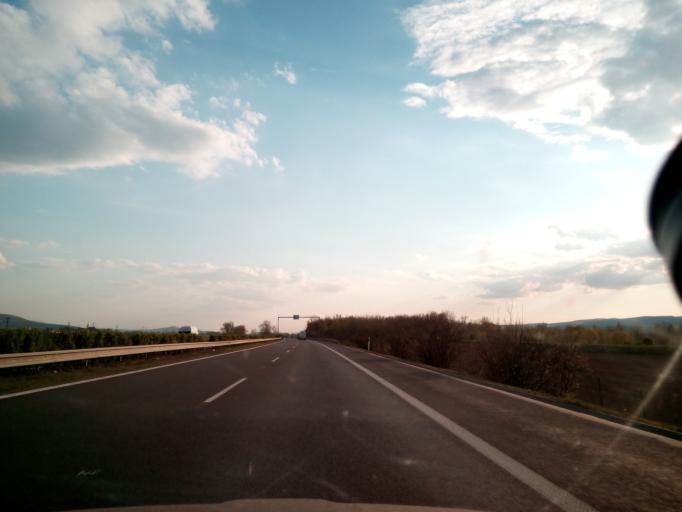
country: SK
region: Nitriansky
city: Ilava
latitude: 49.0158
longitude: 18.2507
